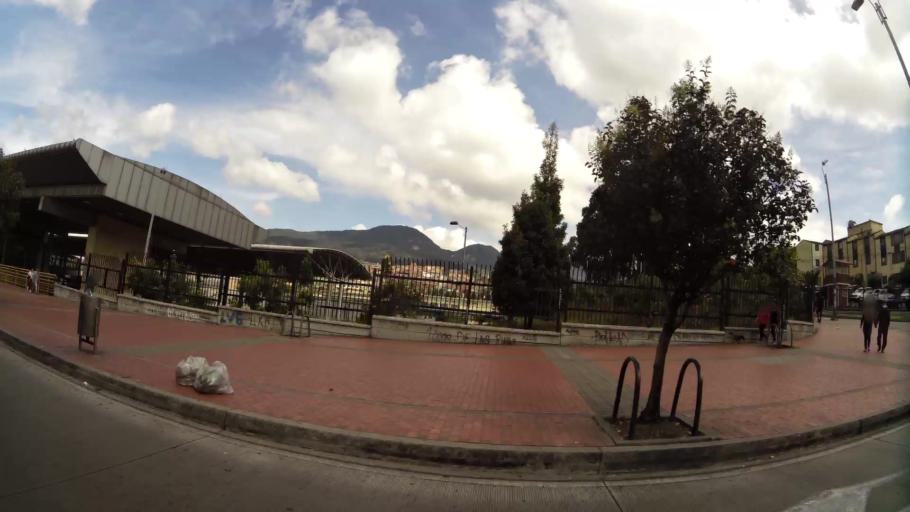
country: CO
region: Bogota D.C.
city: Bogota
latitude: 4.5652
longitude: -74.0985
